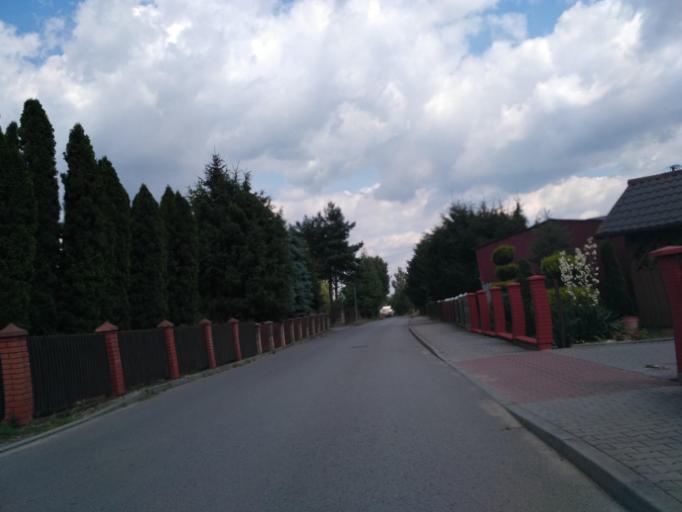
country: PL
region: Subcarpathian Voivodeship
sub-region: Powiat debicki
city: Pilzno
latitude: 49.9708
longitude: 21.2917
